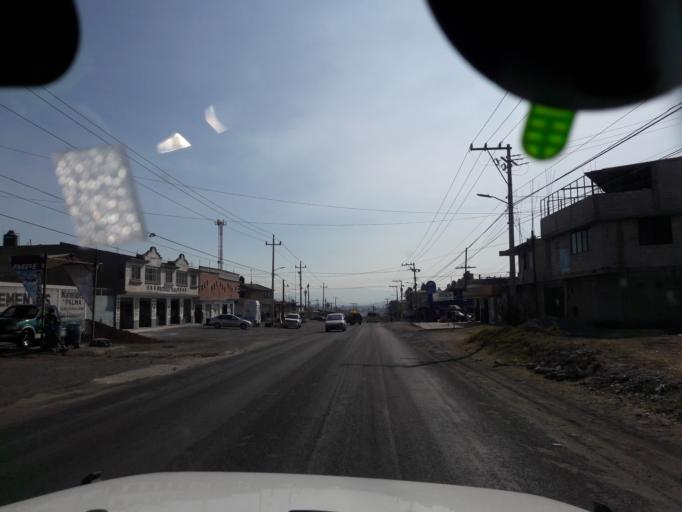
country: MX
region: Puebla
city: San Martin Texmelucan de Labastida
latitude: 19.2947
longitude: -98.4019
